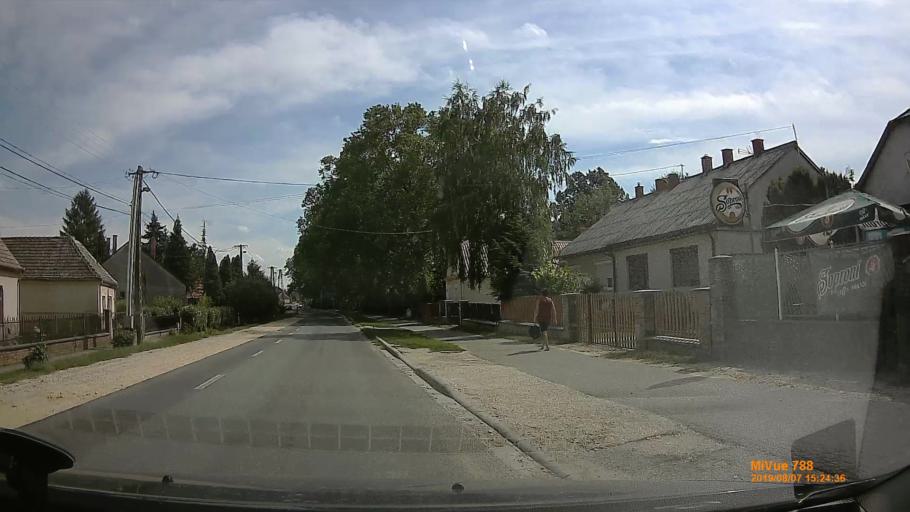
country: HU
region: Vas
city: Buk
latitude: 47.3101
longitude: 16.8326
